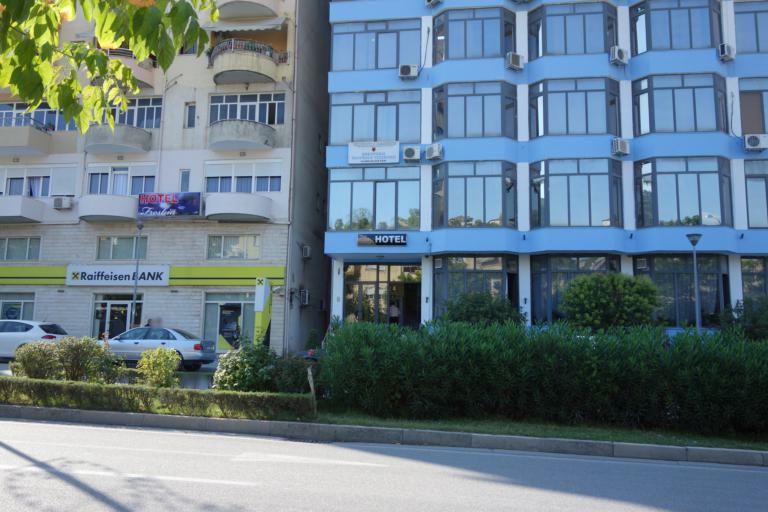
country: AL
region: Gjirokaster
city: Gjirokaster
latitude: 40.0810
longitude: 20.1391
